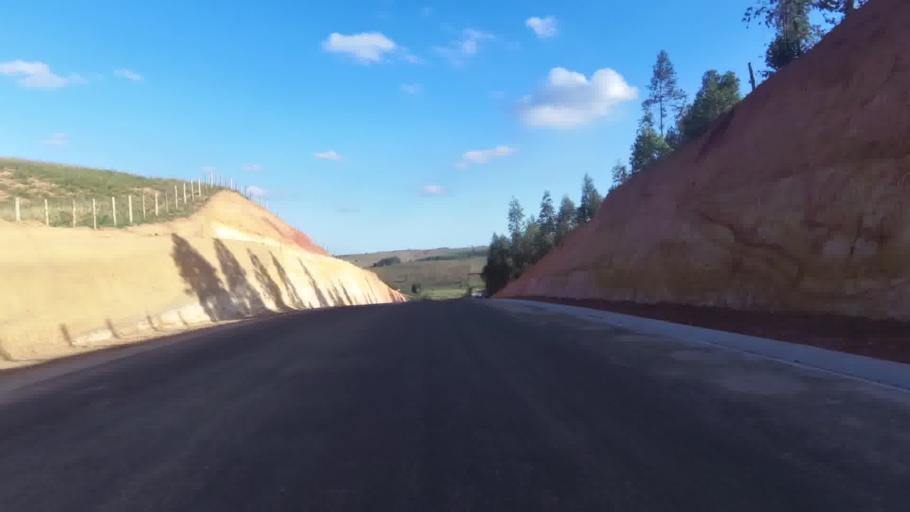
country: BR
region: Espirito Santo
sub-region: Marataizes
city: Marataizes
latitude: -21.1247
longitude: -41.0500
